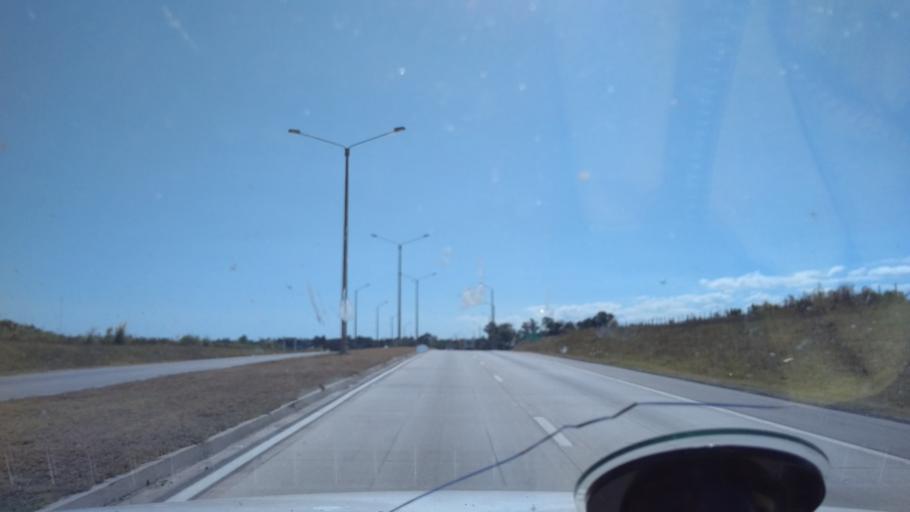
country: UY
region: Canelones
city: Toledo
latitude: -34.7912
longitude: -56.1038
